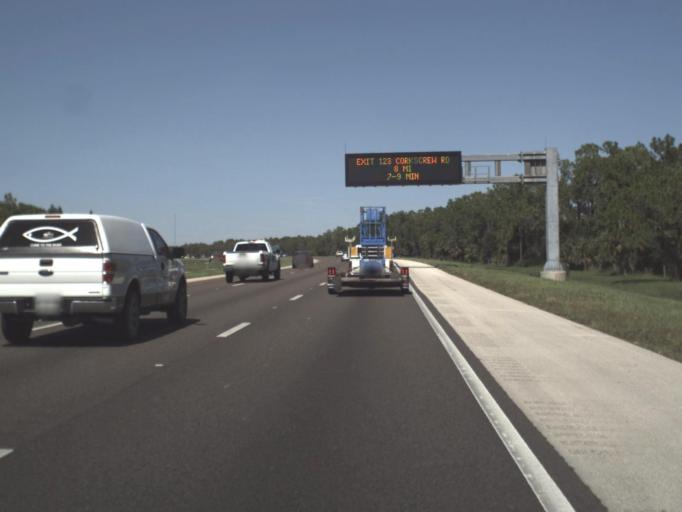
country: US
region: Florida
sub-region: Lee County
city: Bonita Springs
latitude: 26.3050
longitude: -81.7428
